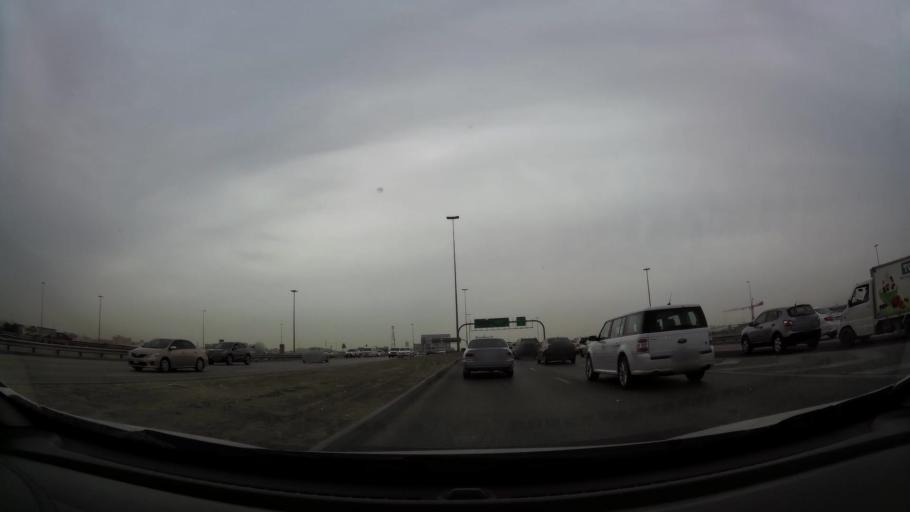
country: BH
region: Manama
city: Jidd Hafs
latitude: 26.1971
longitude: 50.5343
